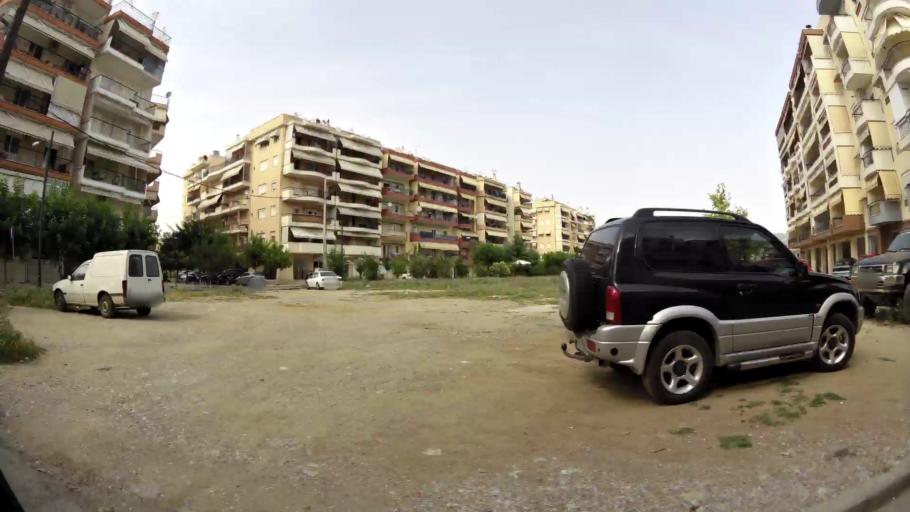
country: GR
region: Central Macedonia
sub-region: Nomos Thessalonikis
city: Stavroupoli
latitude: 40.6841
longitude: 22.9327
